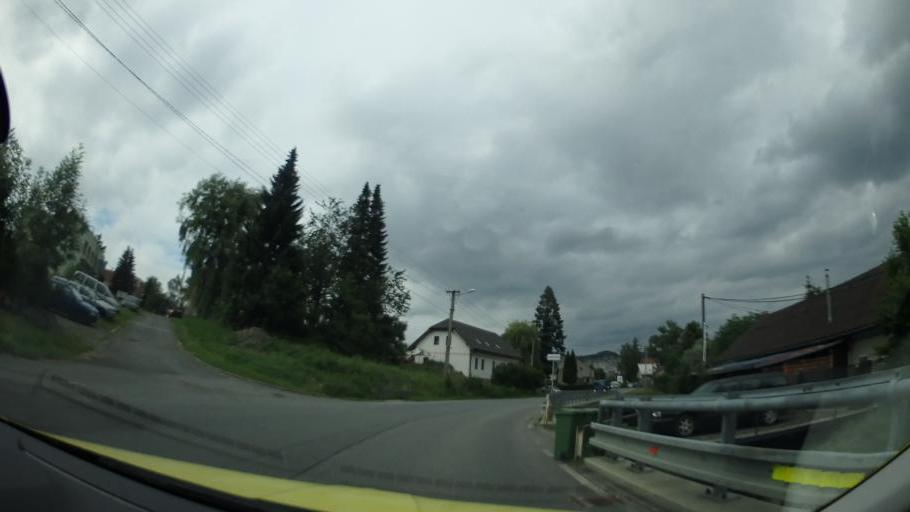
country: CZ
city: Verovice
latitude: 49.5658
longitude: 18.1090
